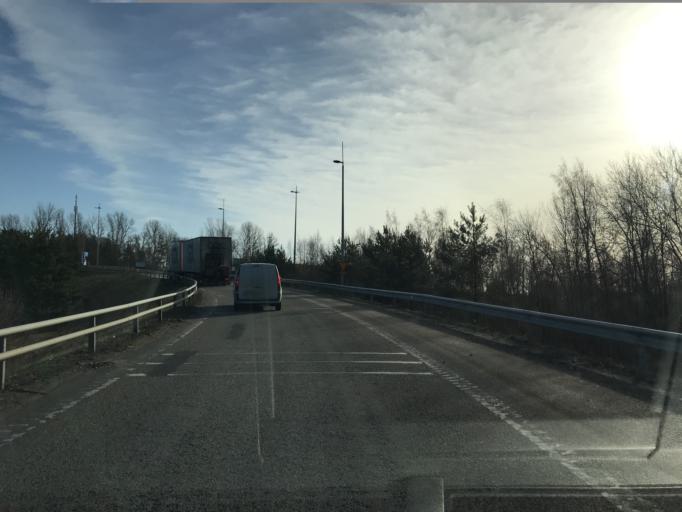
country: SE
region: Skane
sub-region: Kristianstads Kommun
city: Kristianstad
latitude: 56.0176
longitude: 14.1142
